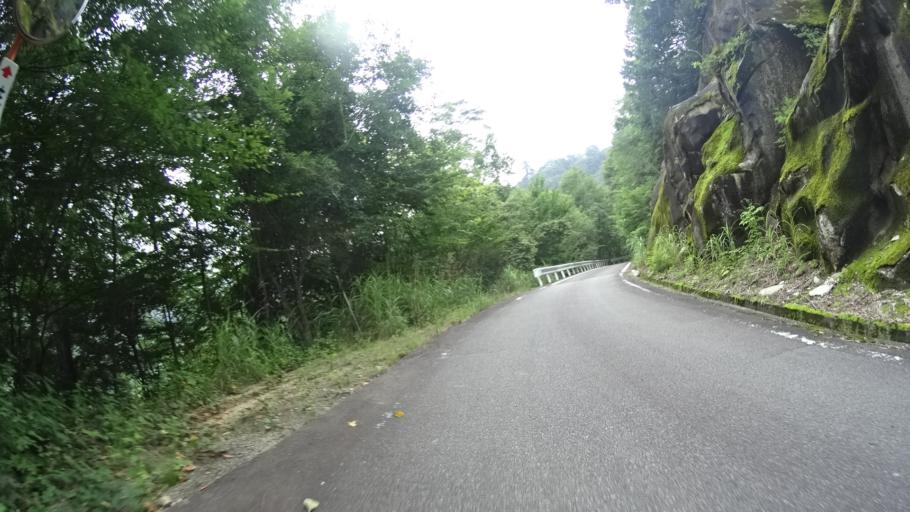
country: JP
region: Yamanashi
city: Kofu-shi
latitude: 35.8091
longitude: 138.6108
